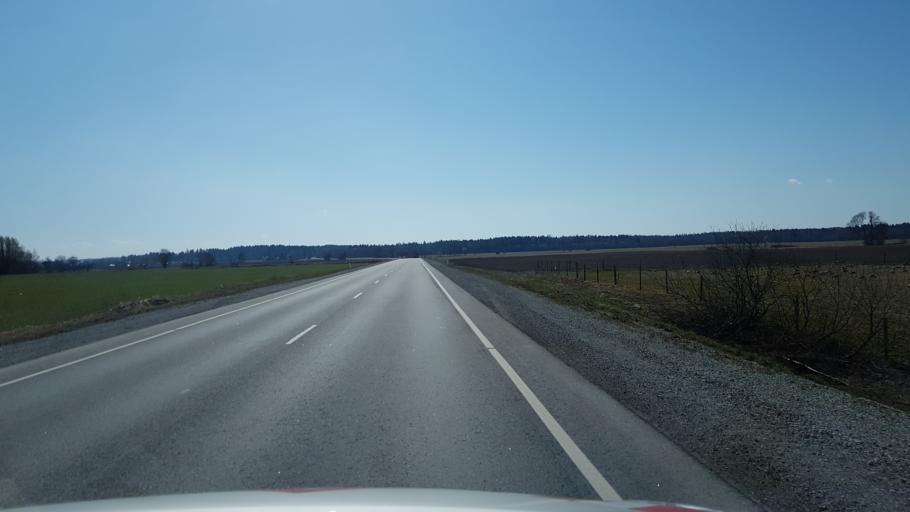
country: EE
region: Ida-Virumaa
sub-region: Kohtla-Jaerve linn
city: Kohtla-Jarve
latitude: 59.3463
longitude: 27.2449
